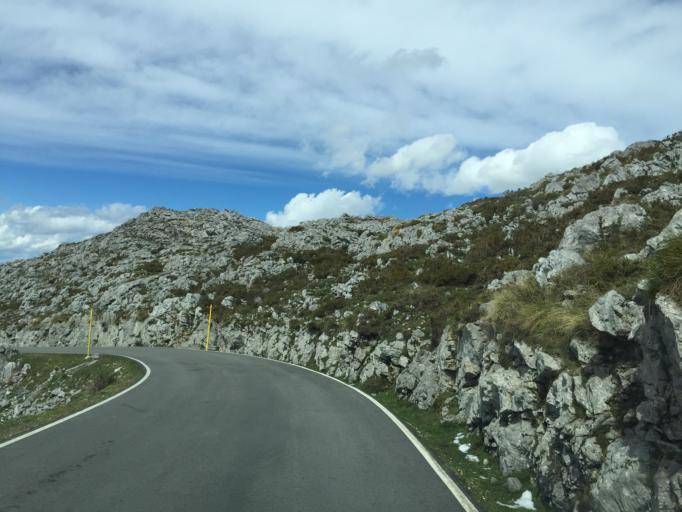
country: ES
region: Asturias
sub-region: Province of Asturias
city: Amieva
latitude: 43.2897
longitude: -5.0049
